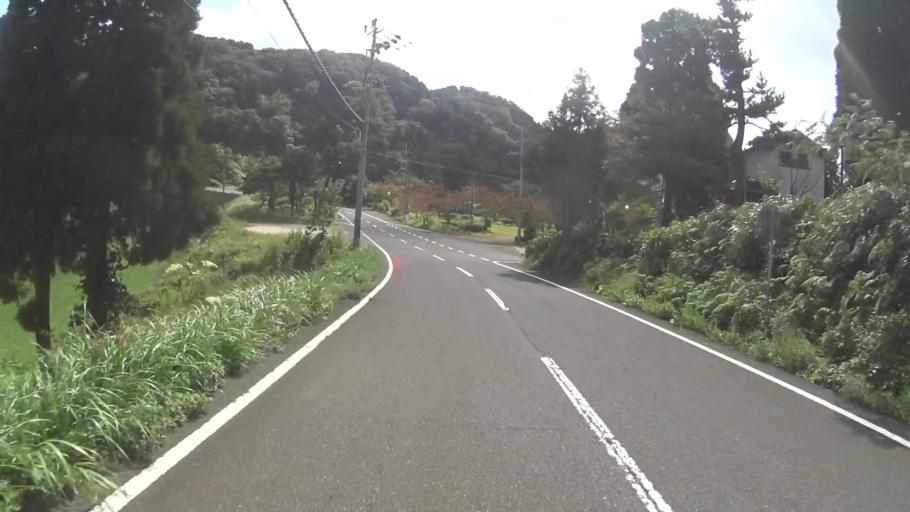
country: JP
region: Kyoto
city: Miyazu
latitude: 35.7205
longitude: 135.1869
